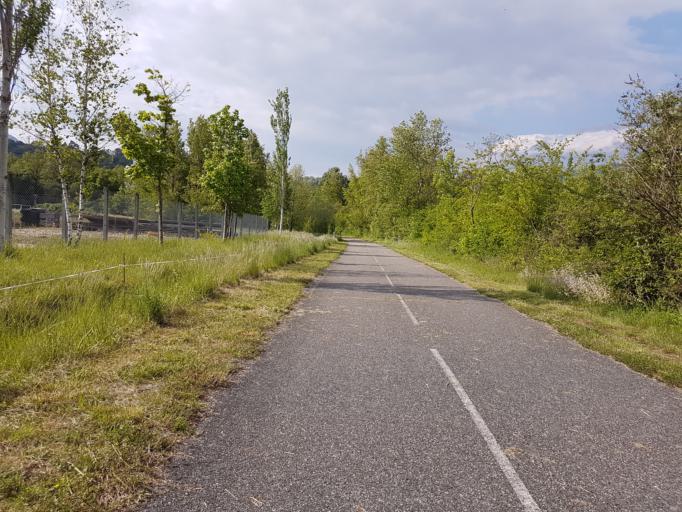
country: FR
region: Rhone-Alpes
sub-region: Departement de la Haute-Savoie
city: Versonnex
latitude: 45.9381
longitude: 5.8335
